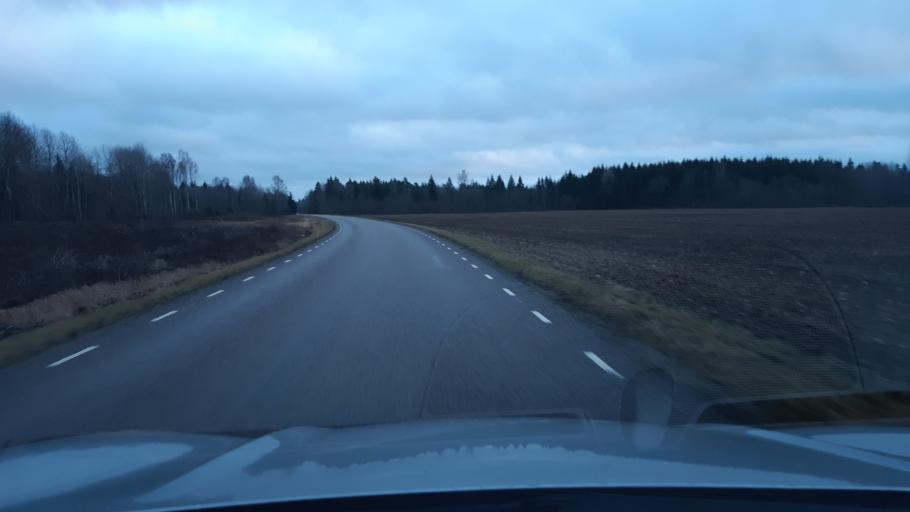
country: EE
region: Raplamaa
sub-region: Kohila vald
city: Kohila
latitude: 59.1416
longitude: 24.6544
